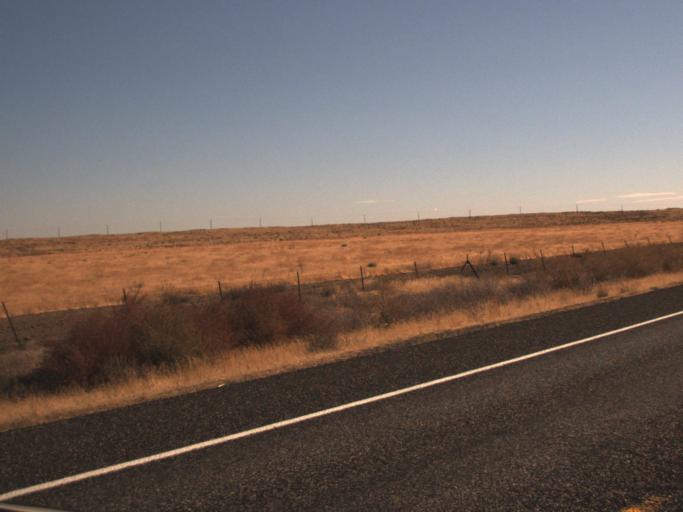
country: US
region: Washington
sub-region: Benton County
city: Benton City
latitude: 46.4729
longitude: -119.5540
